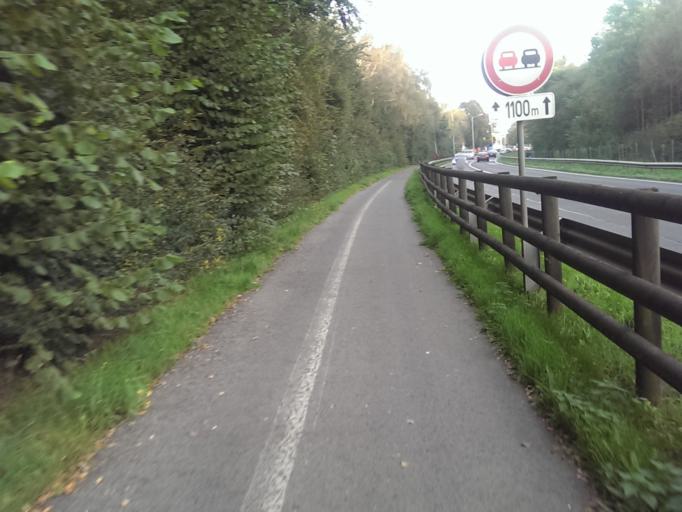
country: AT
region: Styria
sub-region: Graz Stadt
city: Goesting
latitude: 47.1072
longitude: 15.4117
